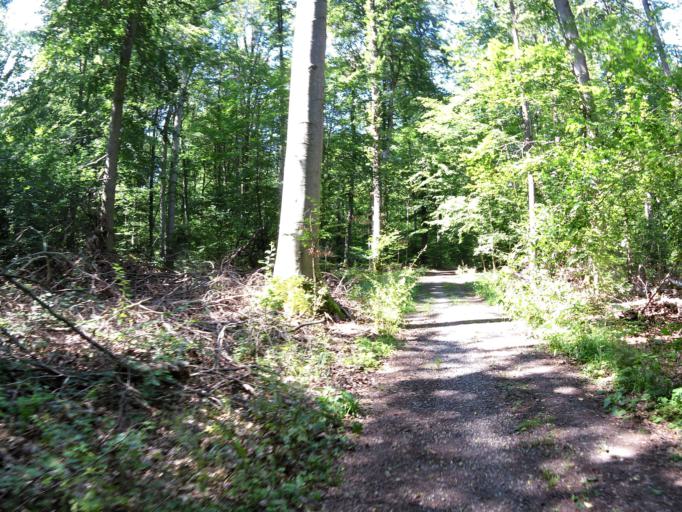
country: DE
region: Bavaria
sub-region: Regierungsbezirk Unterfranken
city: Gadheim
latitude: 49.8512
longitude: 9.8943
